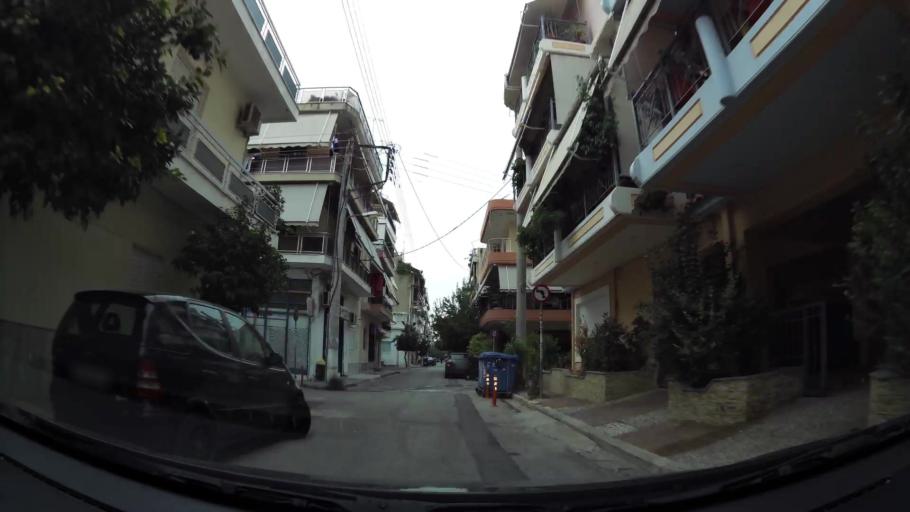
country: GR
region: Attica
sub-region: Nomos Piraios
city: Agios Ioannis Rentis
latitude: 37.9691
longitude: 23.6616
